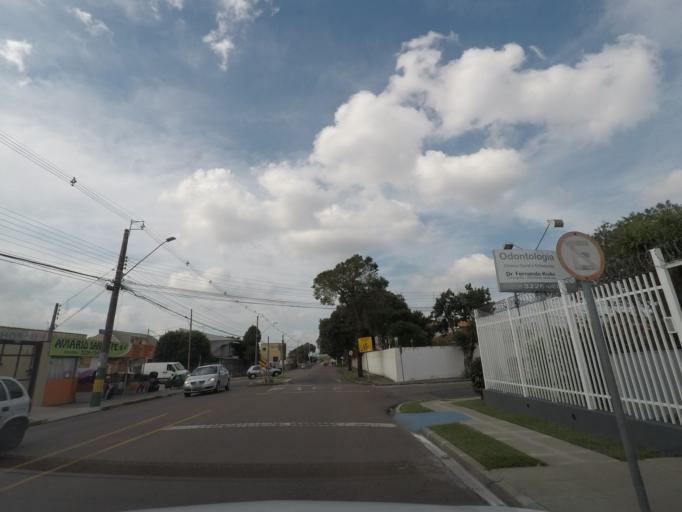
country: BR
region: Parana
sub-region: Pinhais
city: Pinhais
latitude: -25.4691
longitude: -49.2037
